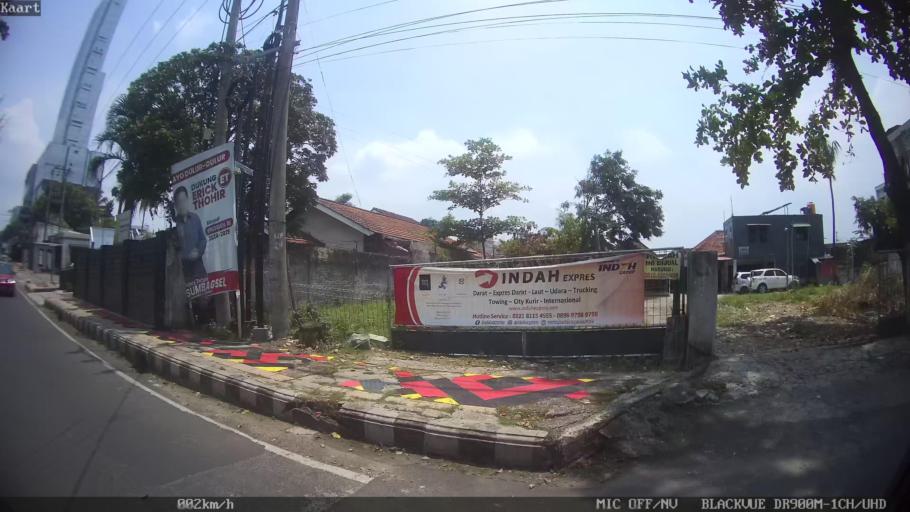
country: ID
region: Lampung
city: Bandarlampung
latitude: -5.4180
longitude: 105.2603
